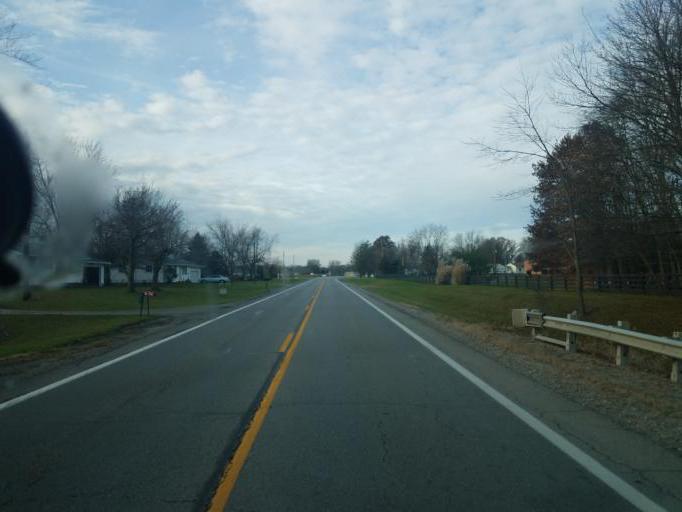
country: US
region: Ohio
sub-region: Morrow County
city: Cardington
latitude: 40.6329
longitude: -82.9634
